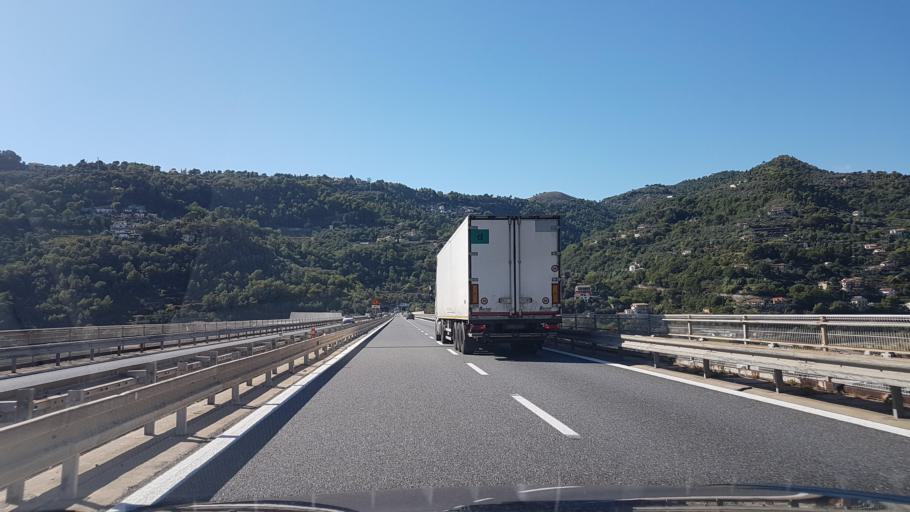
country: IT
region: Liguria
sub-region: Provincia di Imperia
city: Camporosso
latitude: 43.8011
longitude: 7.6322
